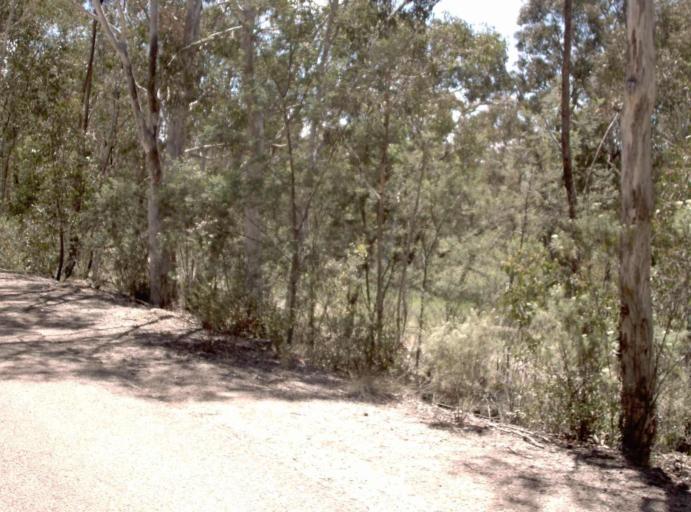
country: AU
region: New South Wales
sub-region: Snowy River
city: Jindabyne
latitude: -37.0418
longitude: 148.2763
